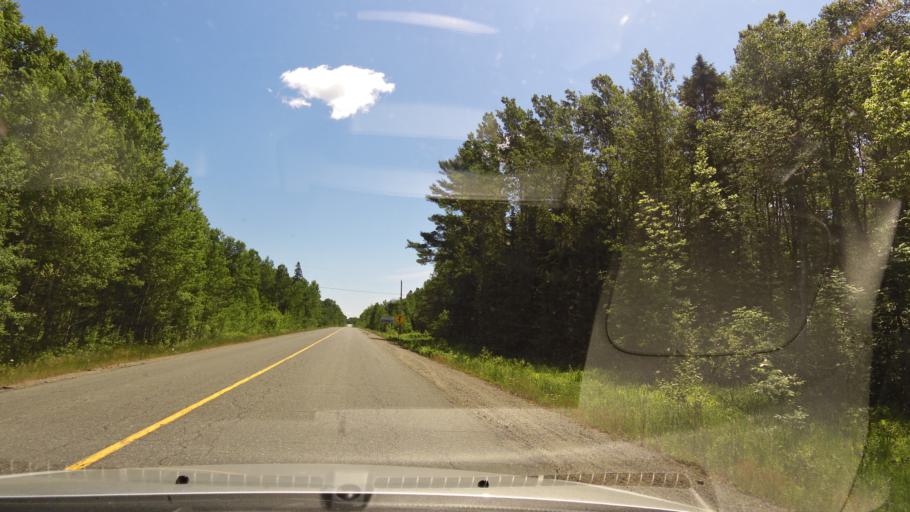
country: CA
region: Ontario
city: Greater Sudbury
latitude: 45.9130
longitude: -80.5637
